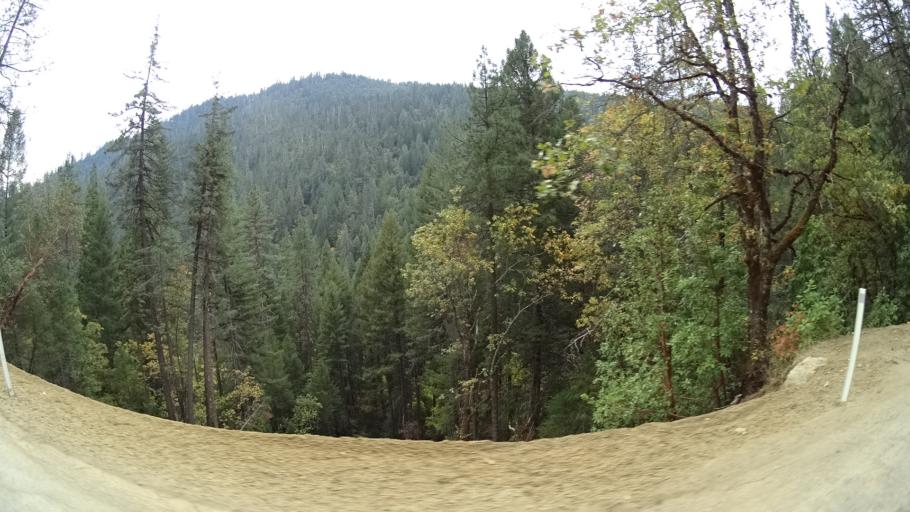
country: US
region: California
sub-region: Siskiyou County
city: Happy Camp
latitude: 41.7735
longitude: -123.3767
